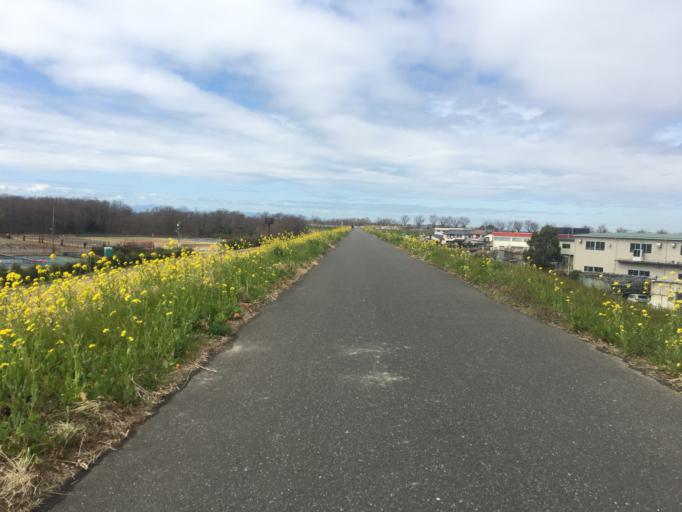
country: JP
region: Saitama
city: Shiki
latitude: 35.8577
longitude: 139.6007
